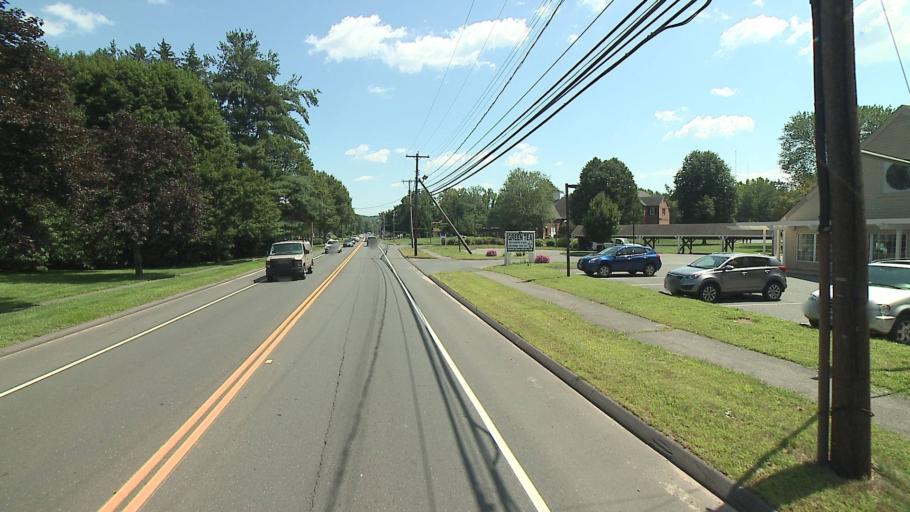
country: US
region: Connecticut
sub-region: Hartford County
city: Farmington
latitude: 41.7357
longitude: -72.8393
